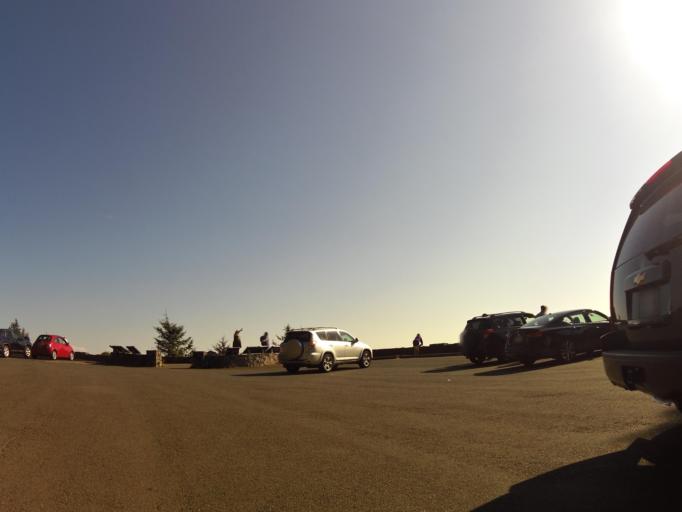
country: US
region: Oregon
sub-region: Tillamook County
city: Rockaway Beach
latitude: 45.7447
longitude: -123.9607
